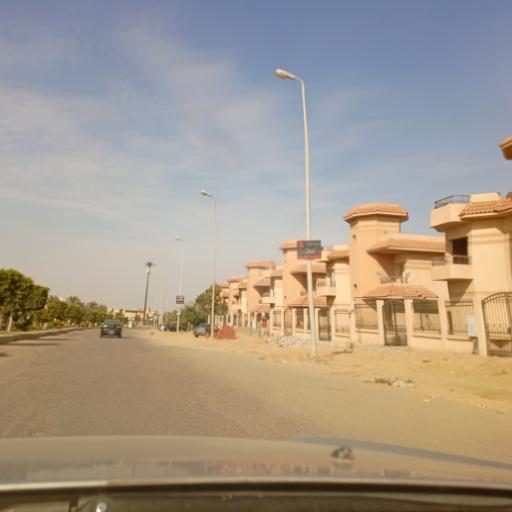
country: EG
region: Muhafazat al Qalyubiyah
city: Al Khankah
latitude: 30.0509
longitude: 31.4853
